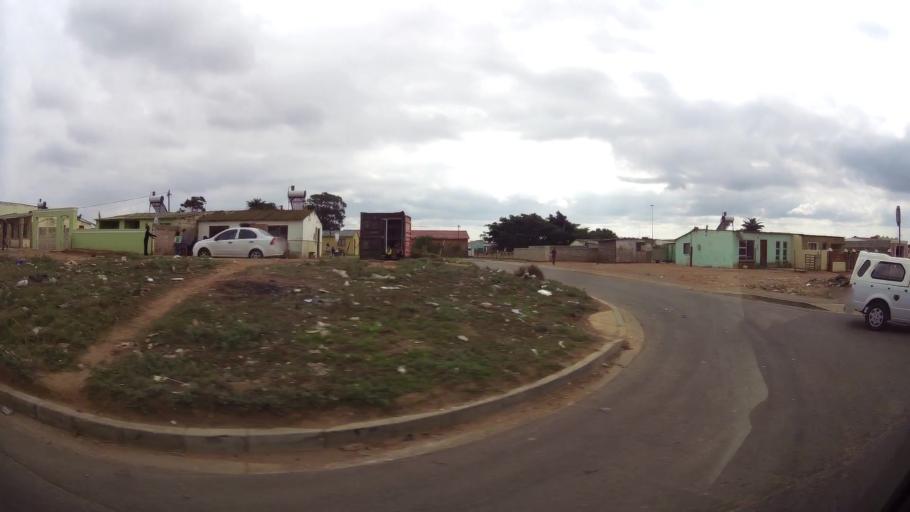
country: ZA
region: Eastern Cape
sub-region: Nelson Mandela Bay Metropolitan Municipality
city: Port Elizabeth
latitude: -33.8673
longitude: 25.5696
